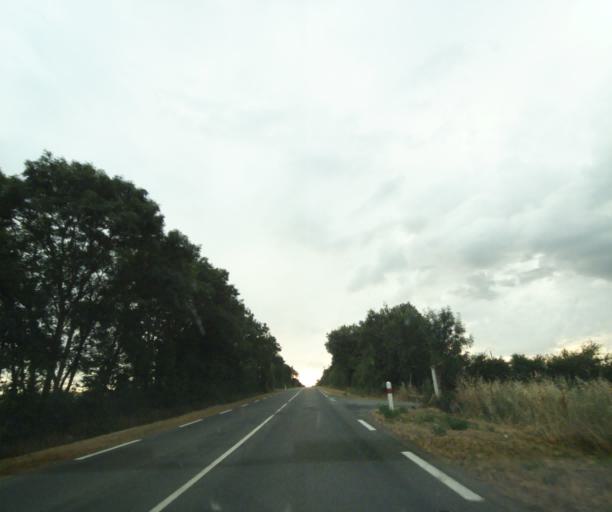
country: FR
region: Pays de la Loire
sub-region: Departement de la Vendee
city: Moutiers-les-Mauxfaits
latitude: 46.4548
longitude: -1.4226
